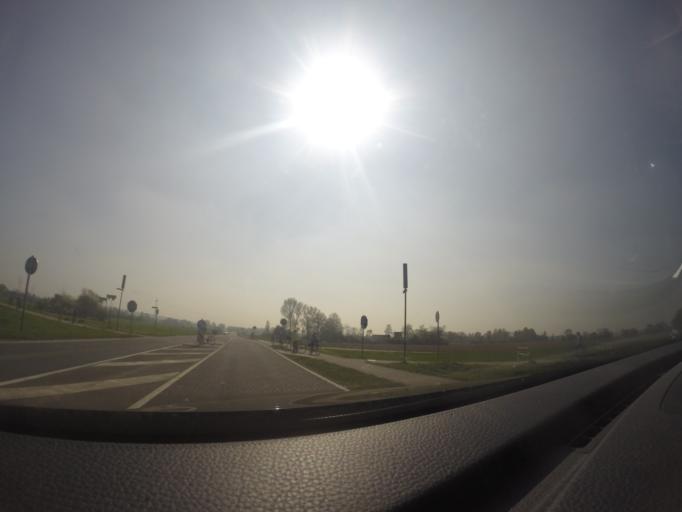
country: DE
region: North Rhine-Westphalia
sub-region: Regierungsbezirk Dusseldorf
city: Xanten
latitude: 51.6683
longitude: 6.4335
